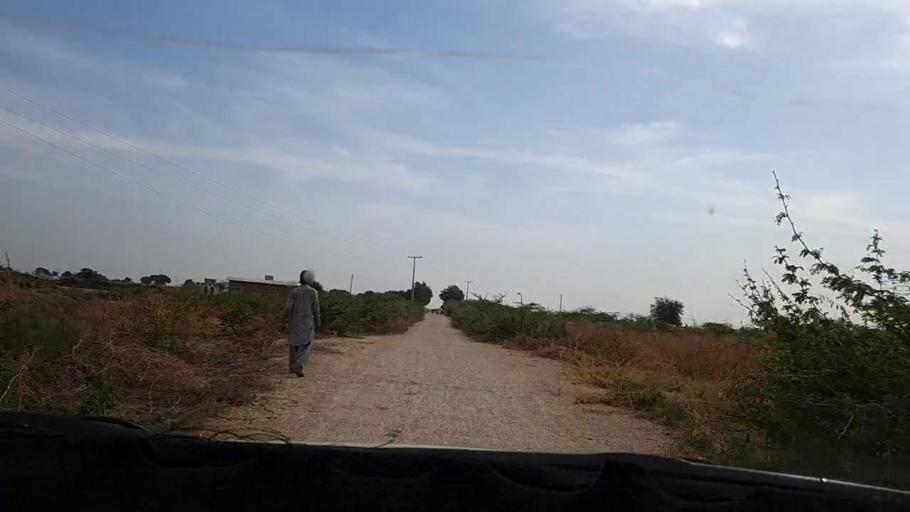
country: PK
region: Sindh
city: Pithoro
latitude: 25.5518
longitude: 69.3297
